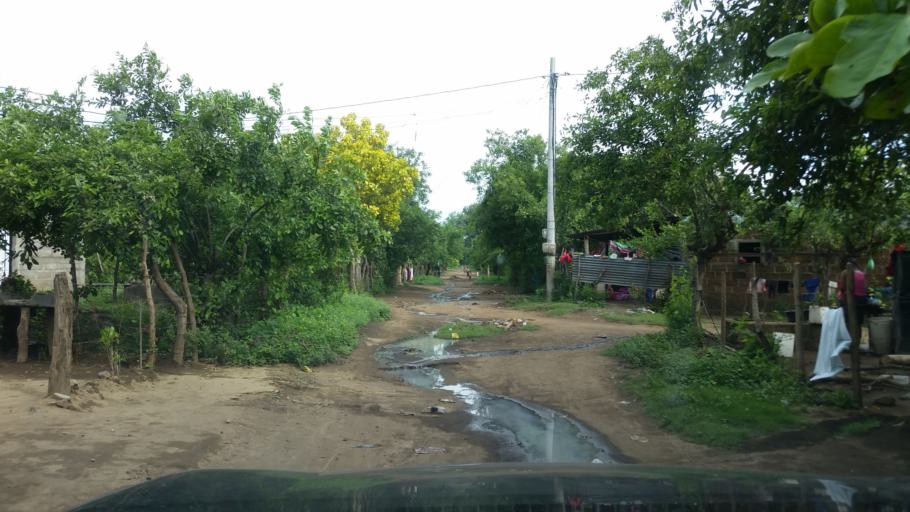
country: NI
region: Chinandega
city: Puerto Morazan
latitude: 12.7645
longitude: -87.1238
